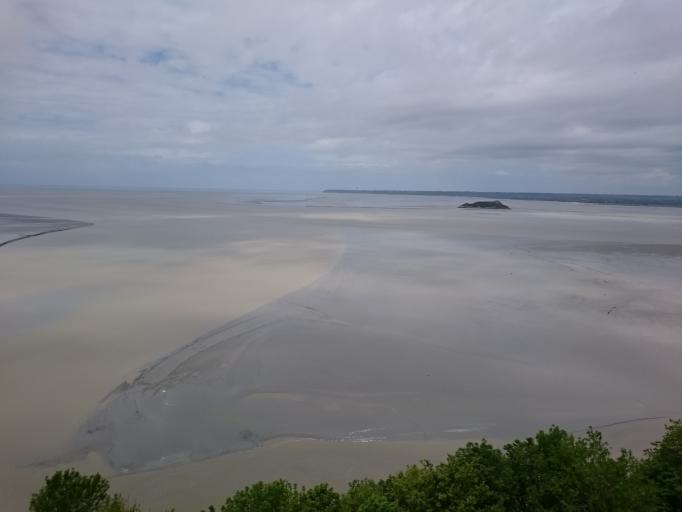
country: FR
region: Lower Normandy
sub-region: Departement de la Manche
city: Pontorson
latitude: 48.6361
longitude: -1.5121
